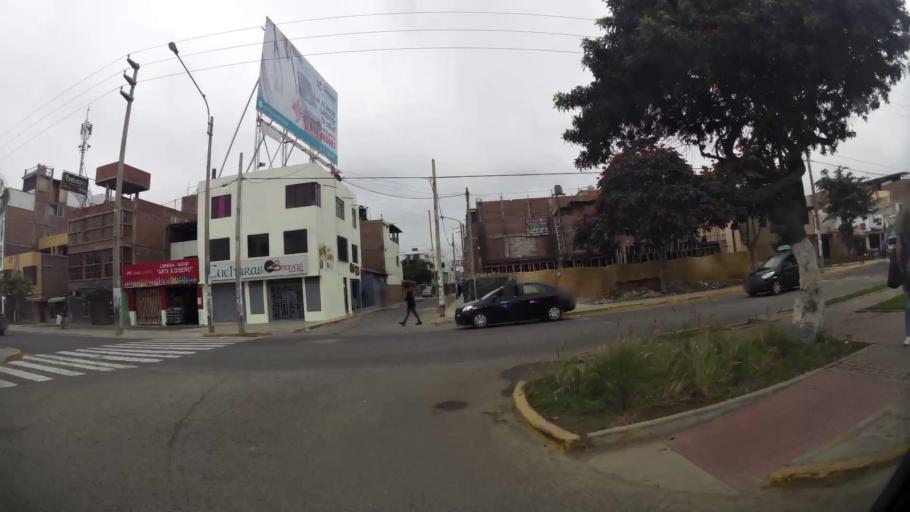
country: PE
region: La Libertad
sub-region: Provincia de Trujillo
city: Trujillo
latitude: -8.1260
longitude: -79.0347
